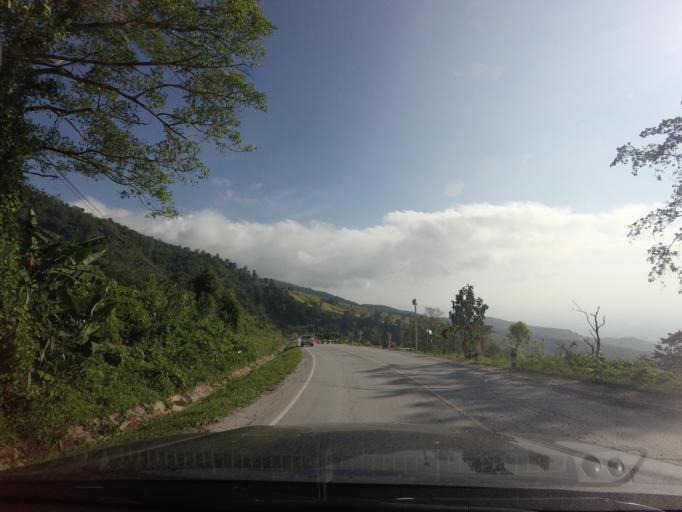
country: TH
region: Phetchabun
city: Lom Kao
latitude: 16.8843
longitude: 101.1198
